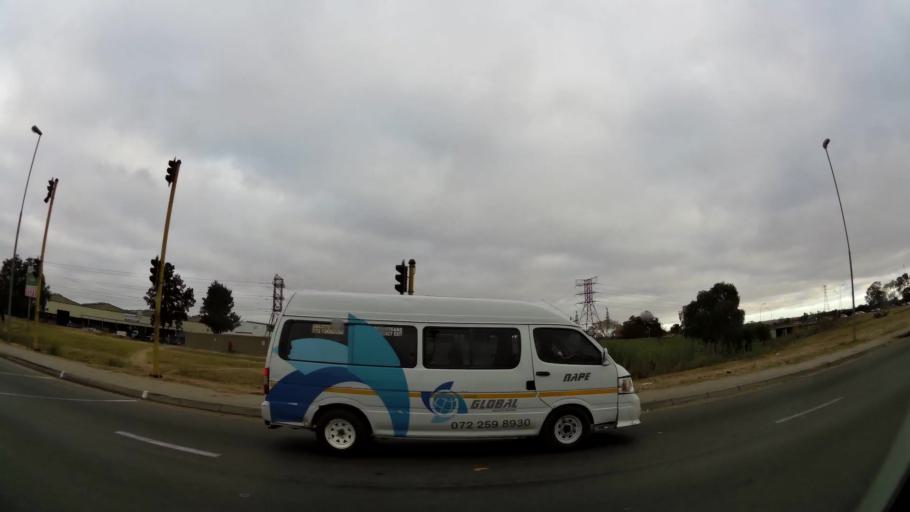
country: ZA
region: Limpopo
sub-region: Capricorn District Municipality
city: Polokwane
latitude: -23.9055
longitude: 29.4419
